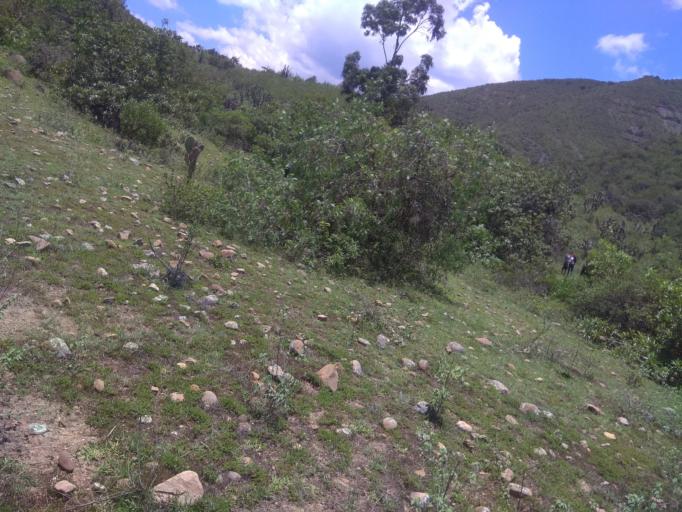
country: CO
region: Boyaca
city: Socha Viejo
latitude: 5.9962
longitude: -72.7188
